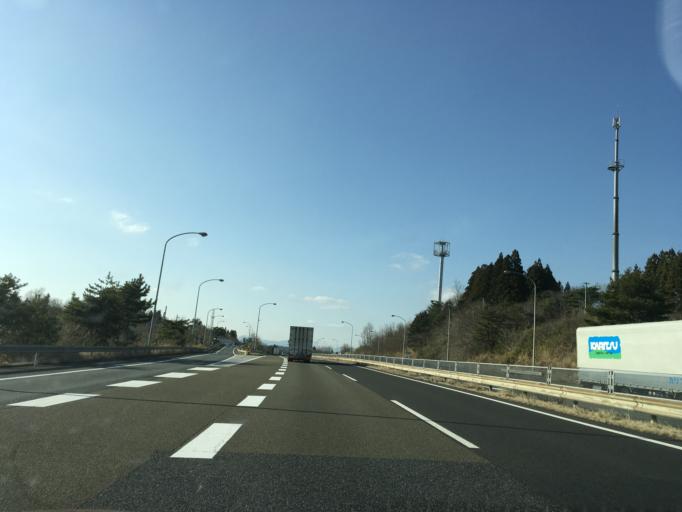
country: JP
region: Iwate
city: Ichinoseki
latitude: 38.8385
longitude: 141.0984
